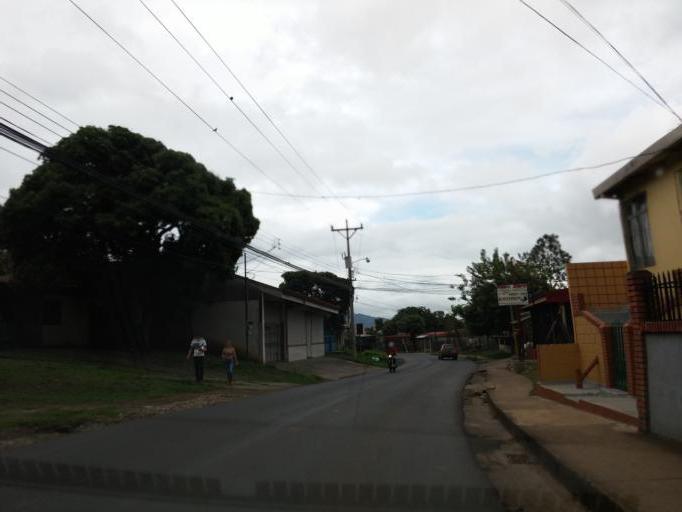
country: CR
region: Alajuela
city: Alajuela
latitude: 10.0056
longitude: -84.2131
